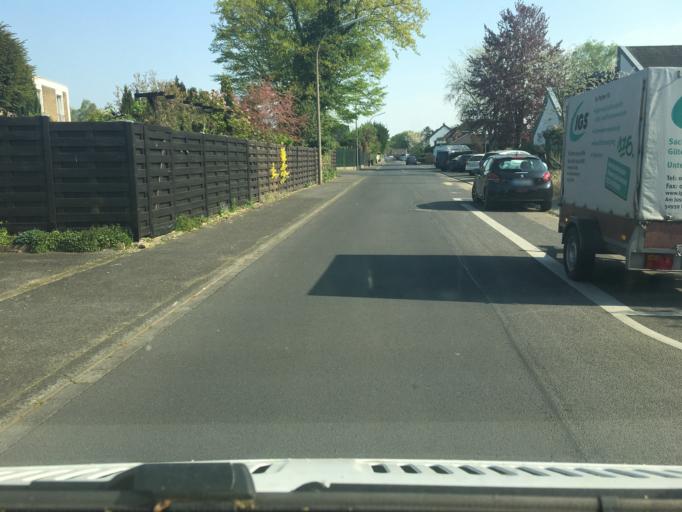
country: DE
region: North Rhine-Westphalia
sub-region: Regierungsbezirk Koln
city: Mengenich
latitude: 50.9693
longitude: 6.8335
